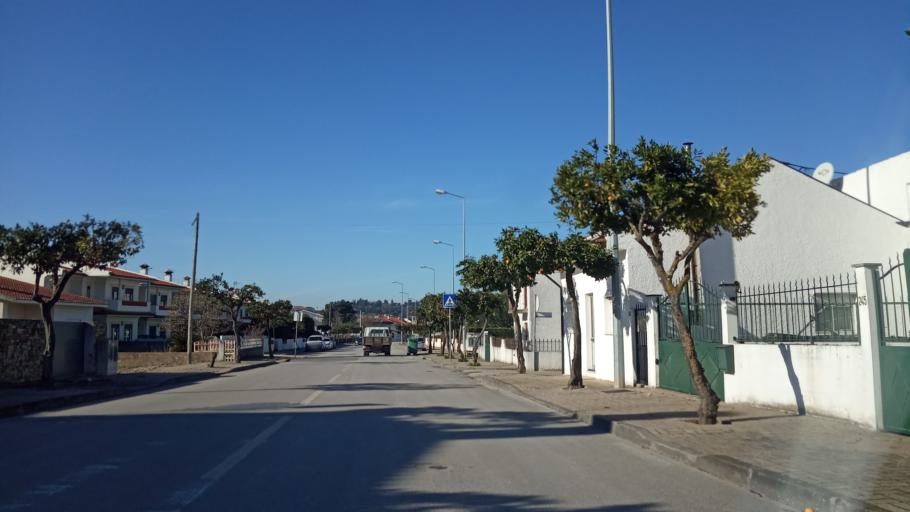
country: PT
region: Aveiro
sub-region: Anadia
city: Anadia
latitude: 40.4353
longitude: -8.4292
